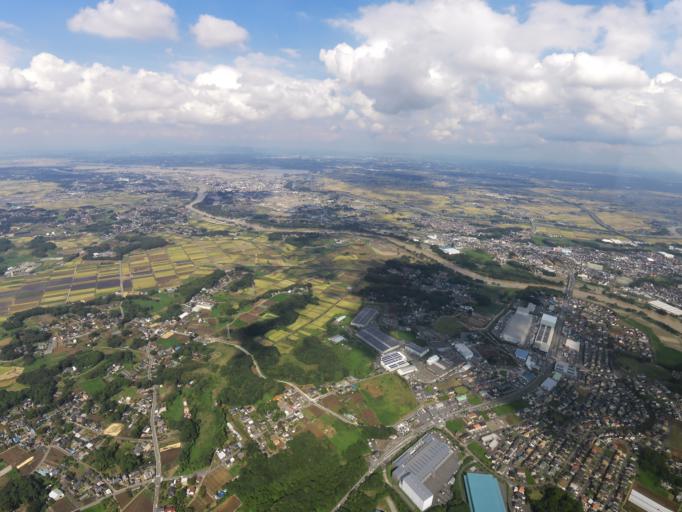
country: JP
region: Ibaraki
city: Mitsukaido
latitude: 35.9816
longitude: 139.9524
